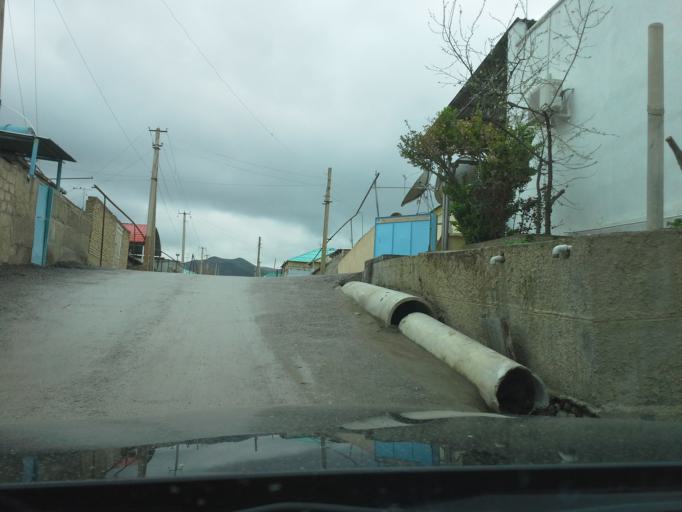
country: TM
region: Ahal
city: Abadan
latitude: 37.9601
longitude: 58.2129
